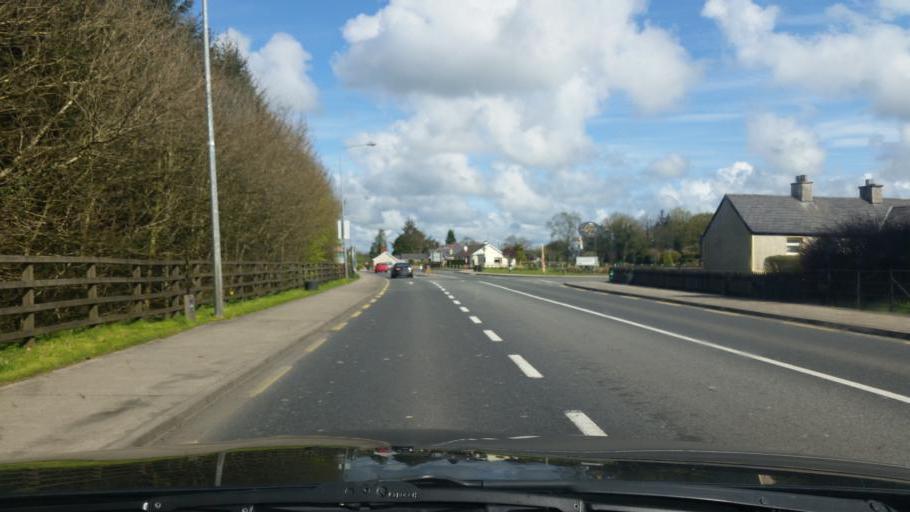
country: IE
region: Ulster
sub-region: An Cabhan
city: Ballyjamesduff
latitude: 53.9658
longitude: -7.2302
